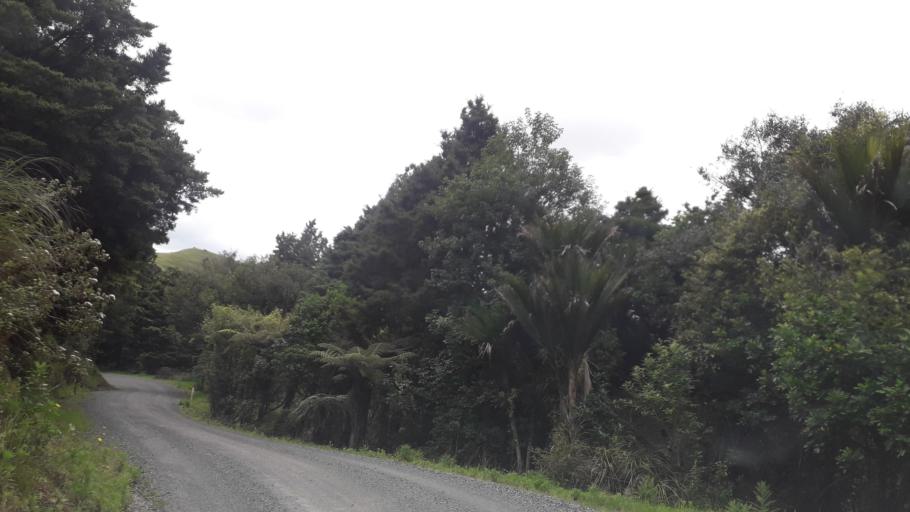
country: NZ
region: Northland
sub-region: Far North District
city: Taipa
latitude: -35.0845
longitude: 173.5499
